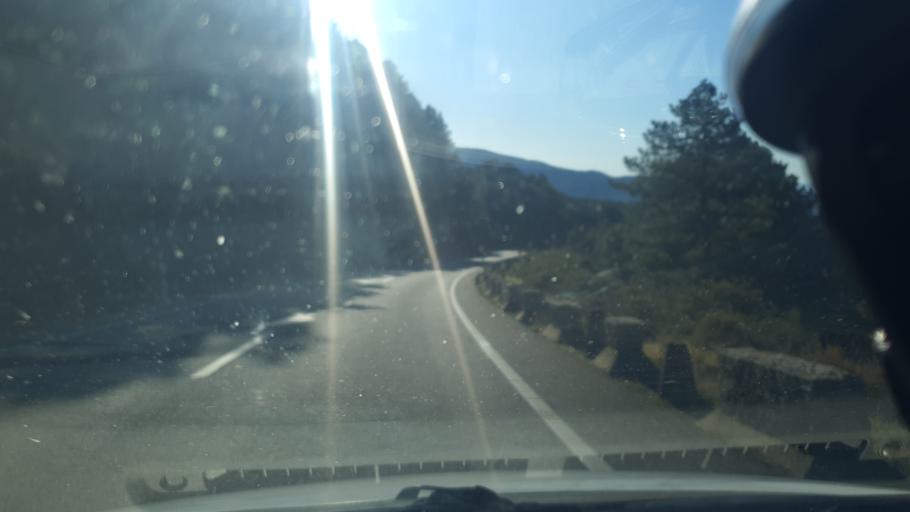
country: ES
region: Castille and Leon
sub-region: Provincia de Avila
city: Cuevas del Valle
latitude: 40.3003
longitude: -5.0077
